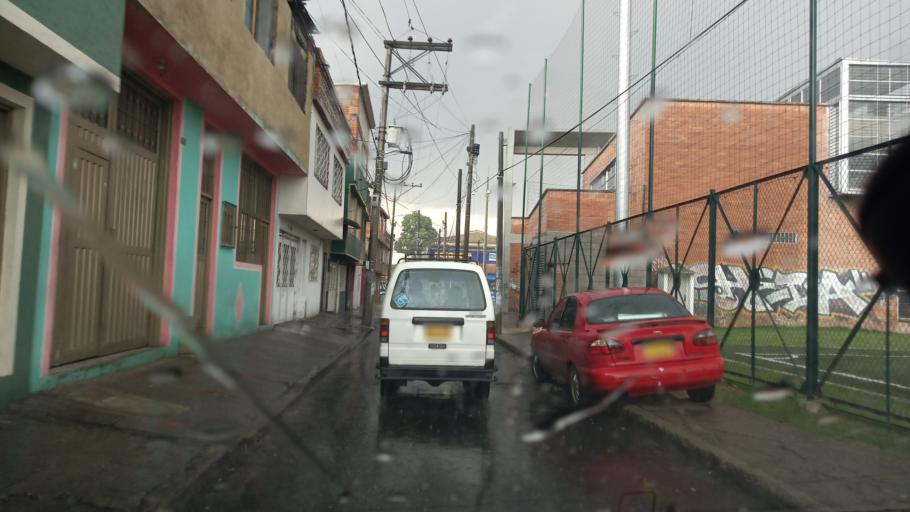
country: CO
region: Cundinamarca
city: Funza
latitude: 4.6728
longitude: -74.1400
